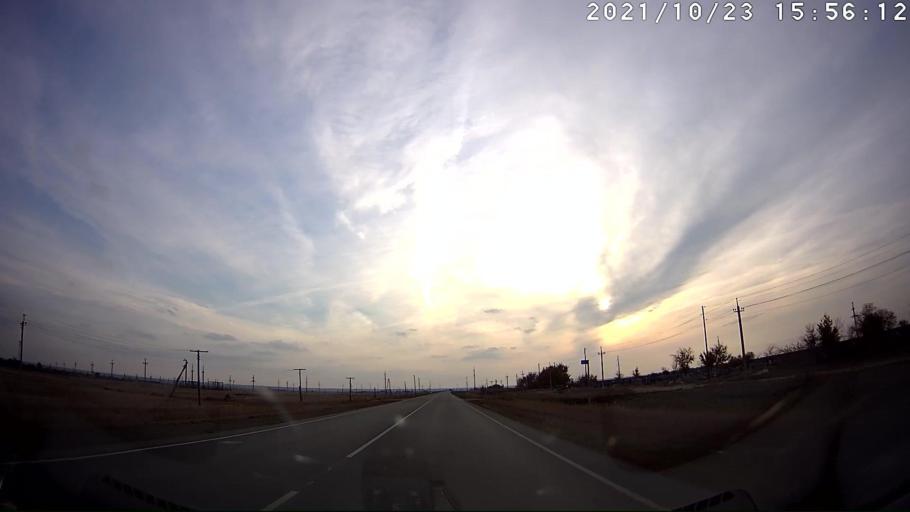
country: RU
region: Kalmykiya
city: Sadovoye
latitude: 47.9612
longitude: 43.9522
